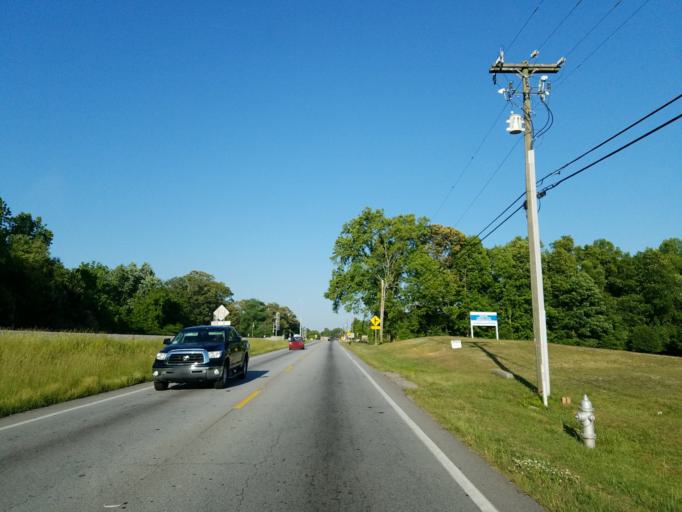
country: US
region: Georgia
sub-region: Douglas County
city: Lithia Springs
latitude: 33.7935
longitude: -84.6682
